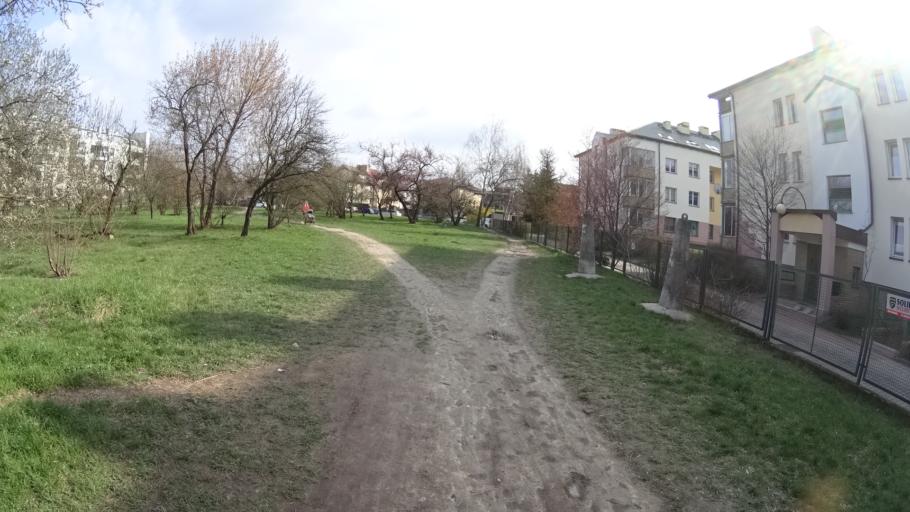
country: PL
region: Masovian Voivodeship
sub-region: Warszawa
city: Bemowo
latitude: 52.2352
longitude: 20.9208
